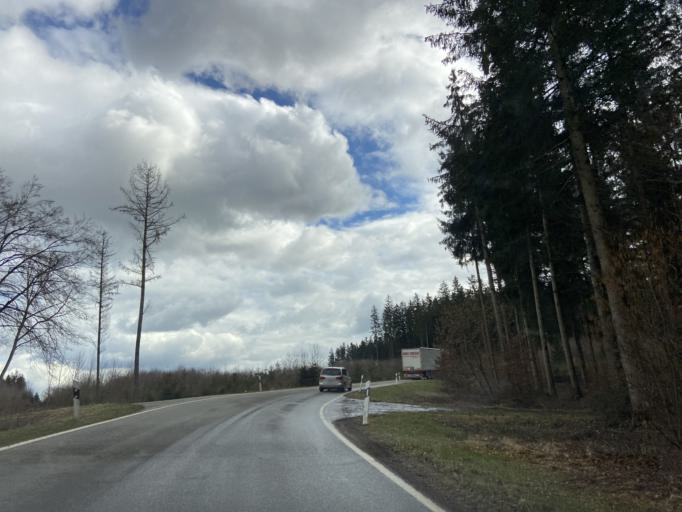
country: DE
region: Baden-Wuerttemberg
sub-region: Tuebingen Region
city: Ostrach
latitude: 47.9564
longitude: 9.3552
